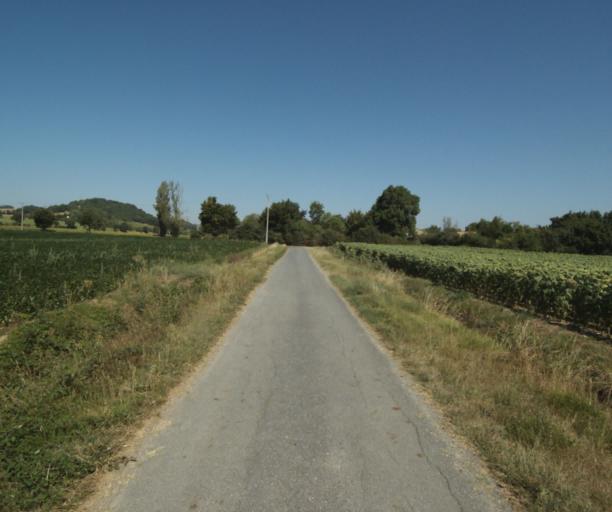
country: FR
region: Midi-Pyrenees
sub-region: Departement de la Haute-Garonne
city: Revel
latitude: 43.5068
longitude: 1.9562
